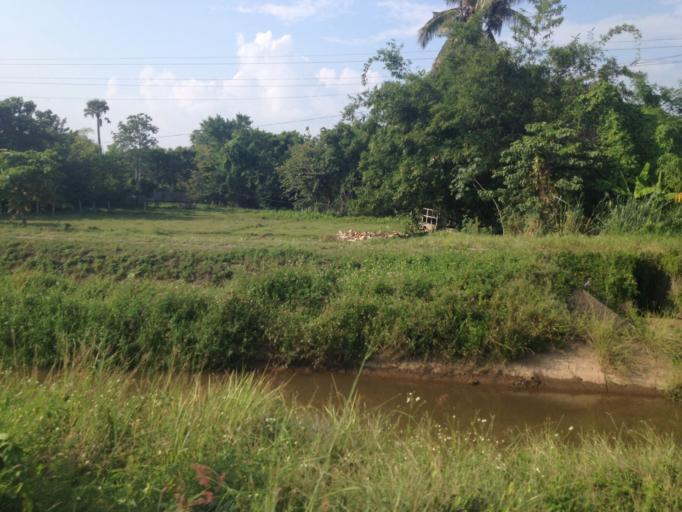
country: TH
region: Chiang Mai
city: Hang Dong
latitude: 18.7101
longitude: 98.9233
